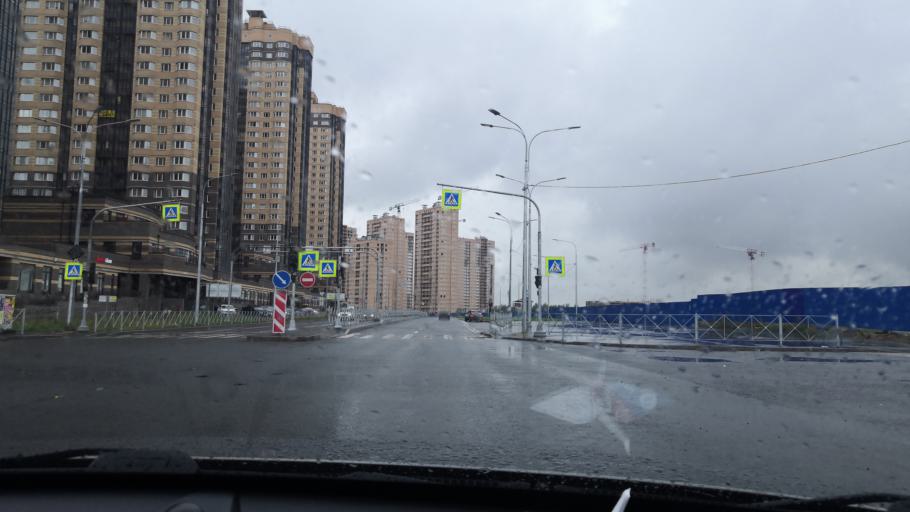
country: RU
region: Leningrad
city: Parnas
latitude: 60.0830
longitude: 30.3553
